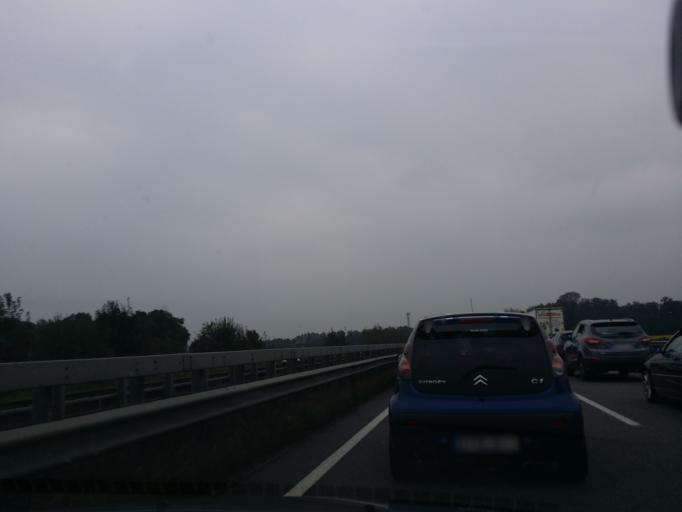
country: DE
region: Lower Saxony
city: Bakum
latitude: 52.7004
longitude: 8.1733
